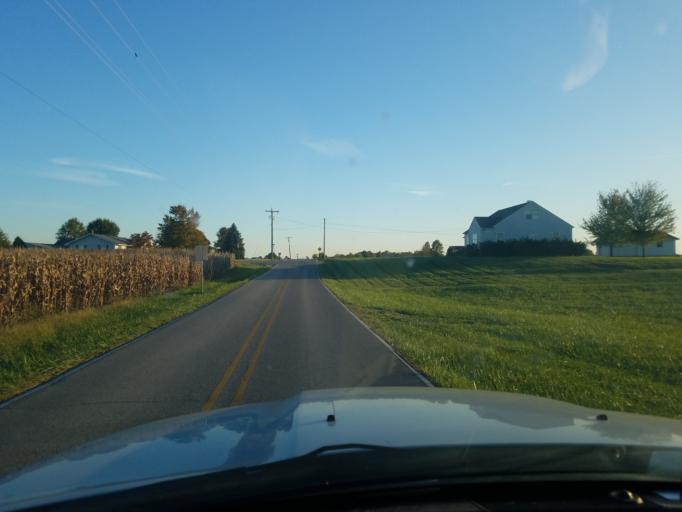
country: US
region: Indiana
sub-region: Floyd County
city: Galena
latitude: 38.4122
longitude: -85.9110
